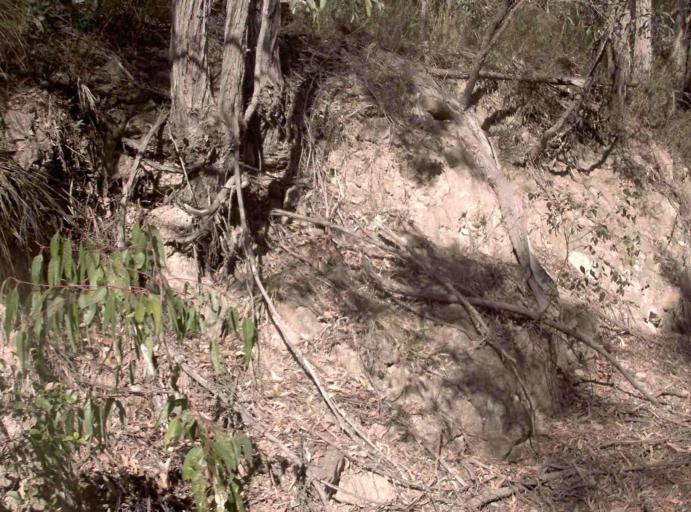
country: AU
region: Victoria
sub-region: East Gippsland
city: Lakes Entrance
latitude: -37.4173
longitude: 148.1229
